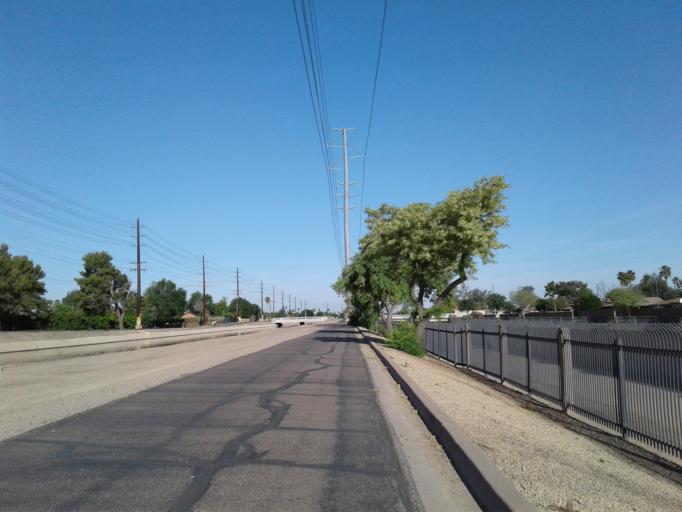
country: US
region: Arizona
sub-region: Maricopa County
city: Glendale
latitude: 33.5713
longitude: -112.1315
